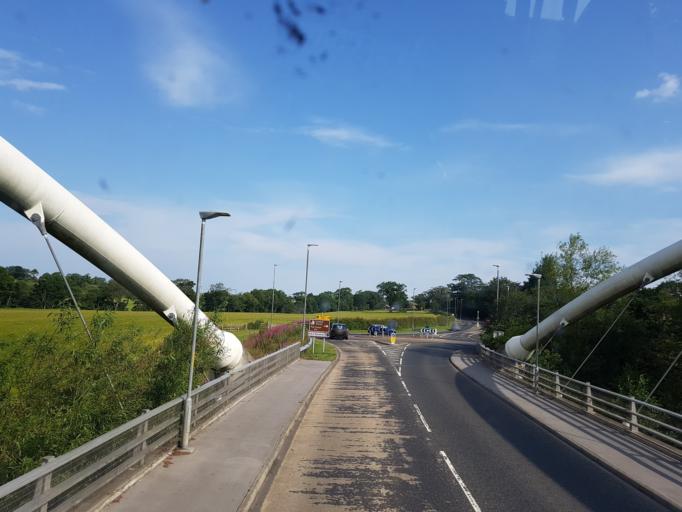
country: GB
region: England
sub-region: Northumberland
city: Alnmouth
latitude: 55.3975
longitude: -1.6348
